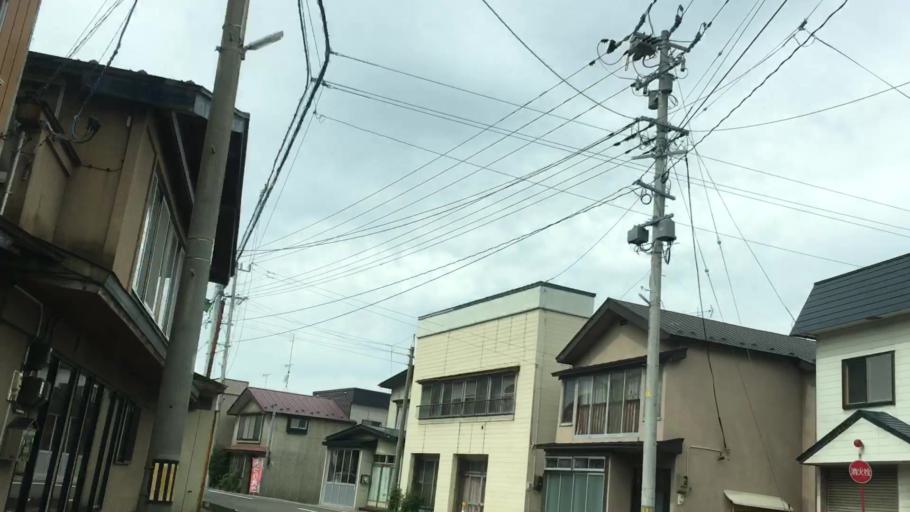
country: JP
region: Aomori
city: Shimokizukuri
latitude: 40.7782
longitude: 140.2167
